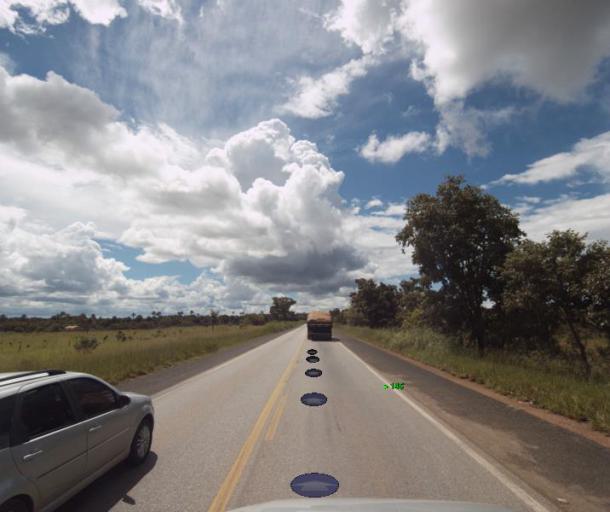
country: BR
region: Goias
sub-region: Uruacu
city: Uruacu
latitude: -14.0424
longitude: -49.0884
